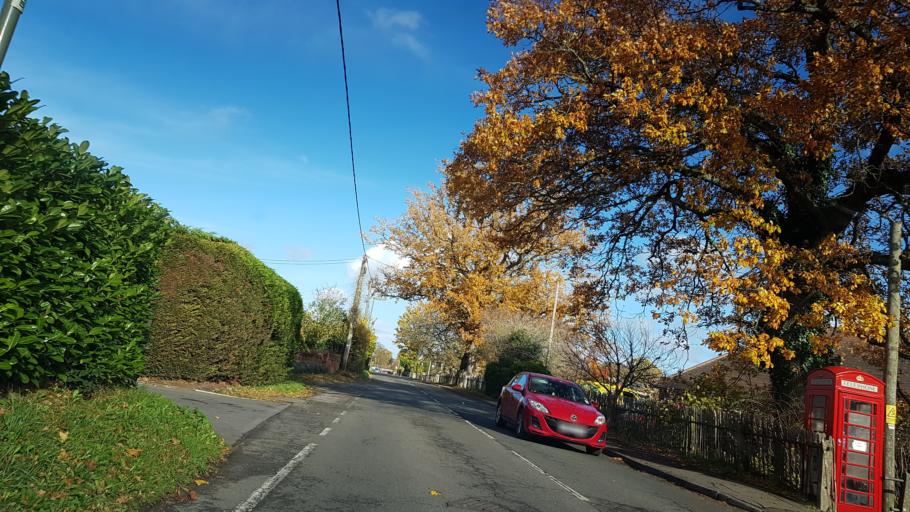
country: GB
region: England
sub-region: Surrey
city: Elstead
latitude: 51.1775
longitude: -0.7111
